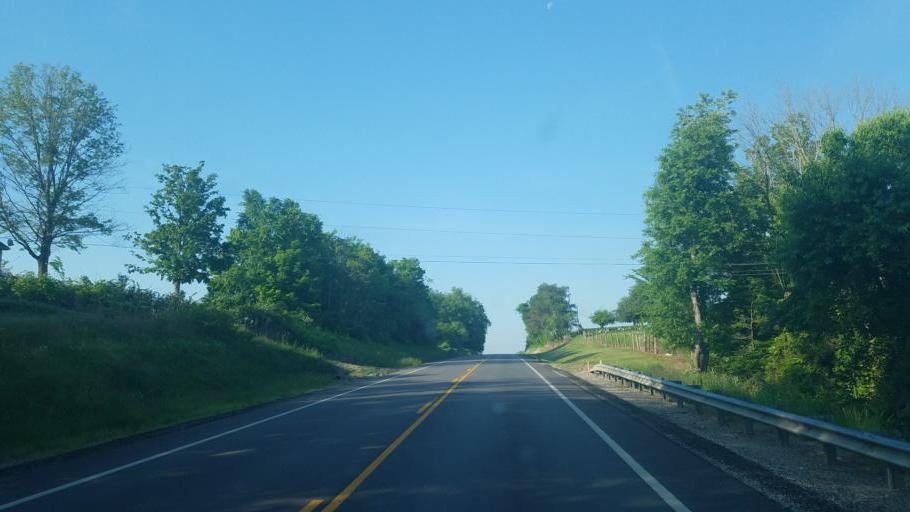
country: US
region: West Virginia
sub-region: Mason County
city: New Haven
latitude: 39.0808
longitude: -81.9279
